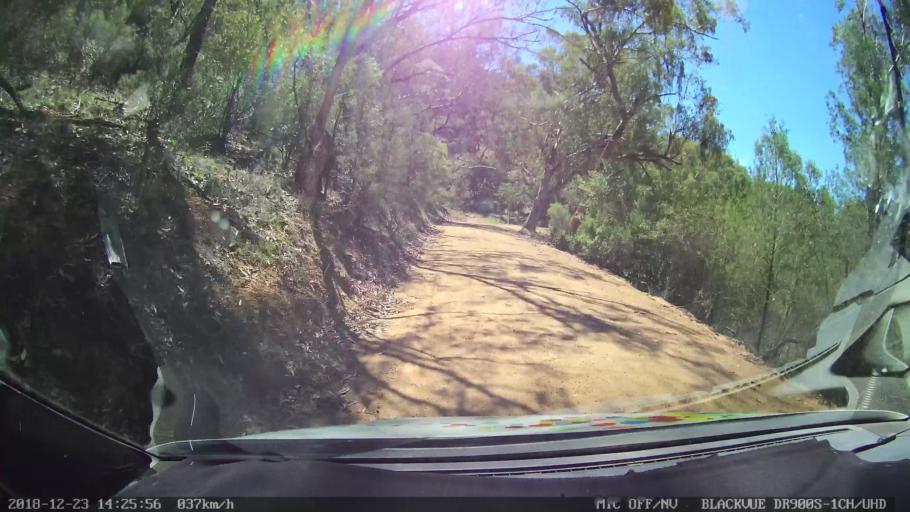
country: AU
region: New South Wales
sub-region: Tamworth Municipality
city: Manilla
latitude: -30.6250
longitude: 150.9539
